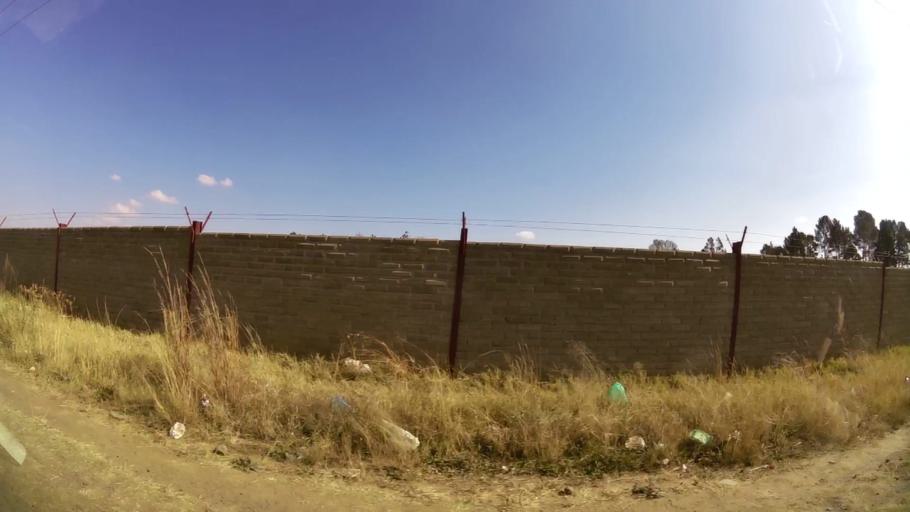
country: ZA
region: Orange Free State
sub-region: Mangaung Metropolitan Municipality
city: Bloemfontein
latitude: -29.1414
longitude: 26.2746
